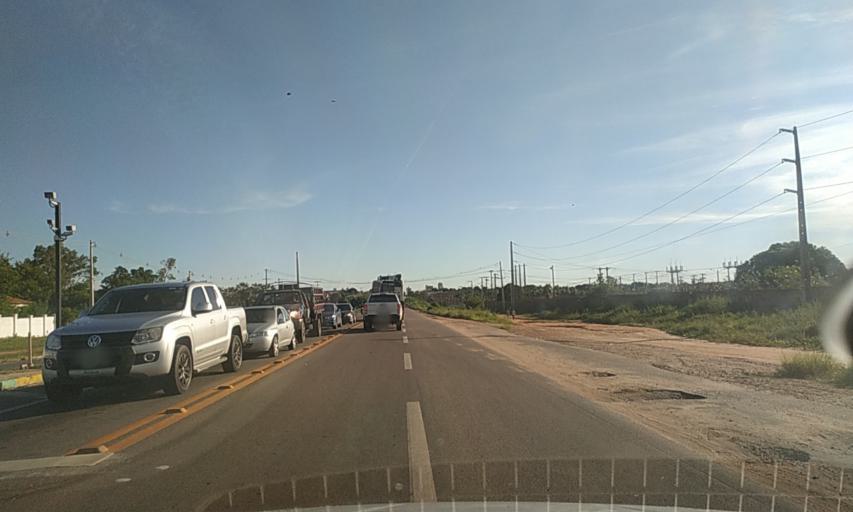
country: BR
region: Rio Grande do Norte
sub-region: Mossoro
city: Mossoro
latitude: -5.1935
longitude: -37.3126
